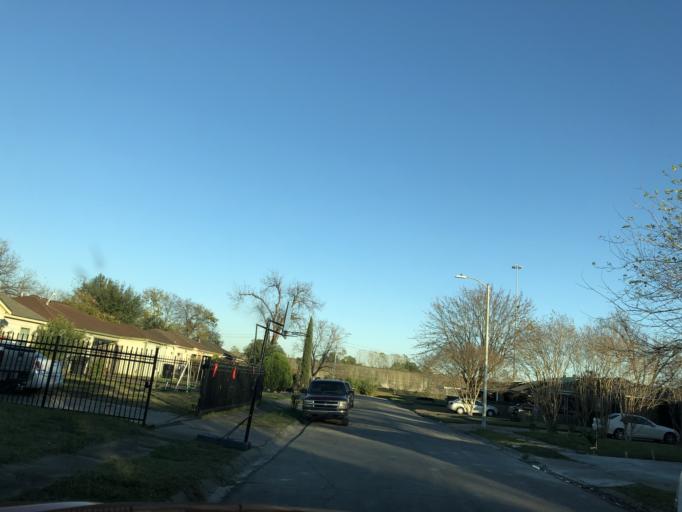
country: US
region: Texas
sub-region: Harris County
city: Jacinto City
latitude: 29.7611
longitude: -95.2672
